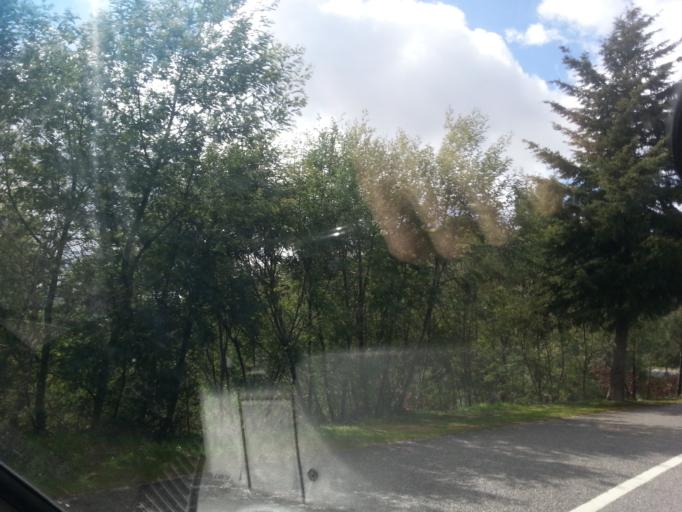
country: PT
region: Guarda
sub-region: Fornos de Algodres
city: Fornos de Algodres
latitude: 40.6143
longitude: -7.4851
